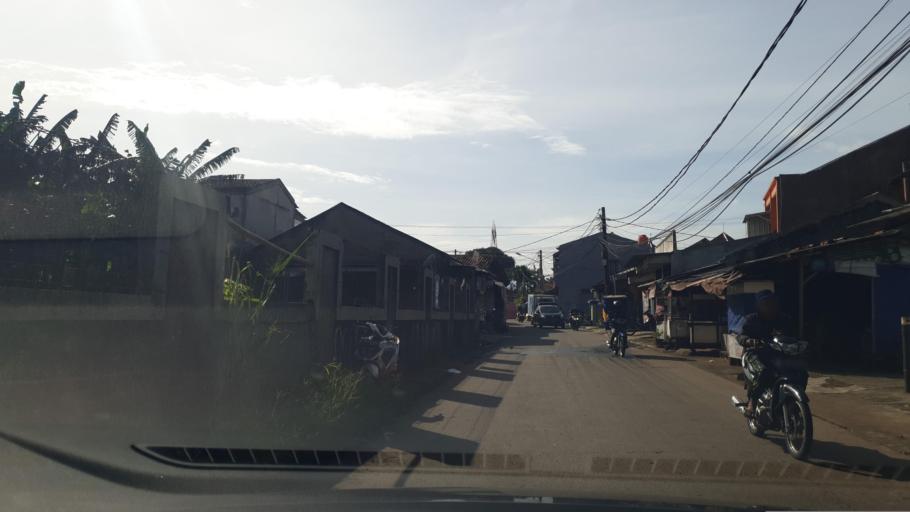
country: ID
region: West Java
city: Sawangan
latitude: -6.3661
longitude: 106.7826
